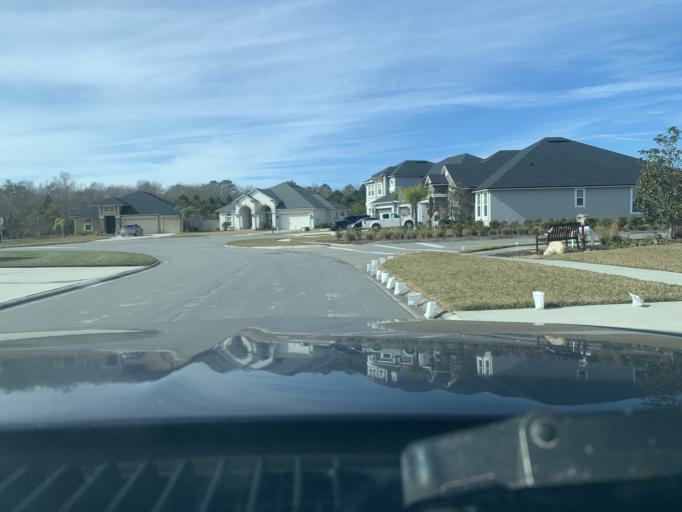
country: US
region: Florida
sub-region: Clay County
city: Green Cove Springs
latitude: 29.9813
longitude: -81.5263
